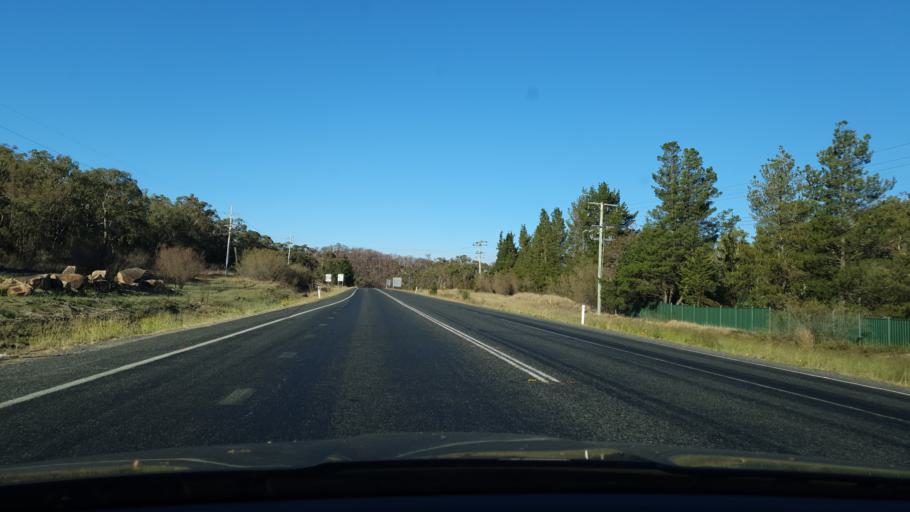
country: AU
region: Queensland
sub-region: Southern Downs
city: Stanthorpe
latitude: -28.6488
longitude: 151.9235
